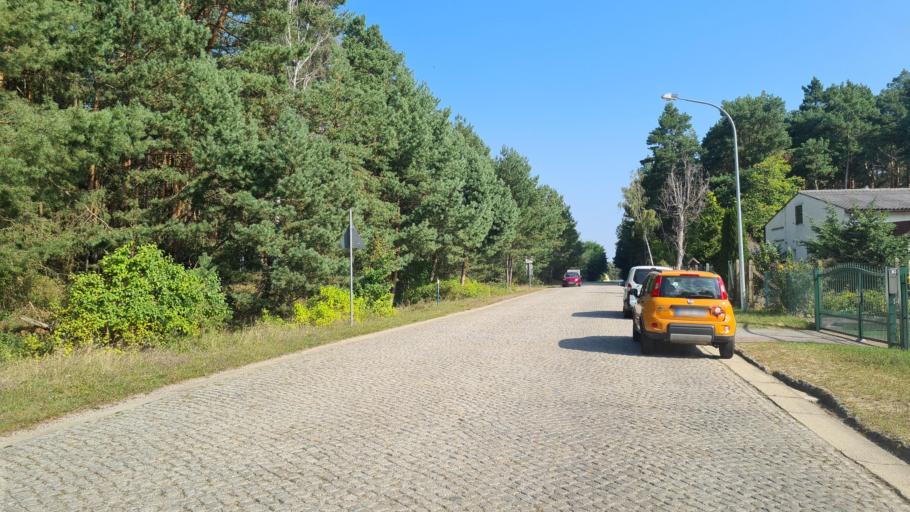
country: DE
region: Brandenburg
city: Kolkwitz
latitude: 51.7180
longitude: 14.2730
